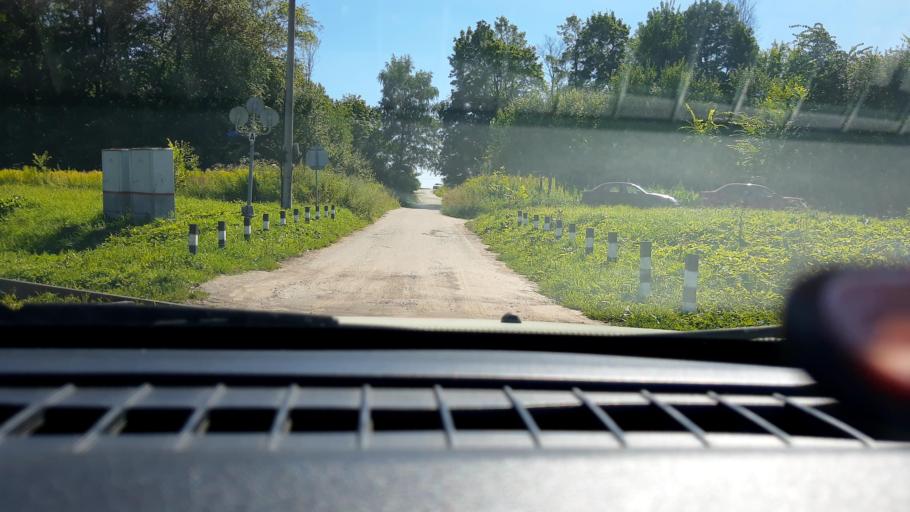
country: RU
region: Nizjnij Novgorod
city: Afonino
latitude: 56.2366
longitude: 44.0461
